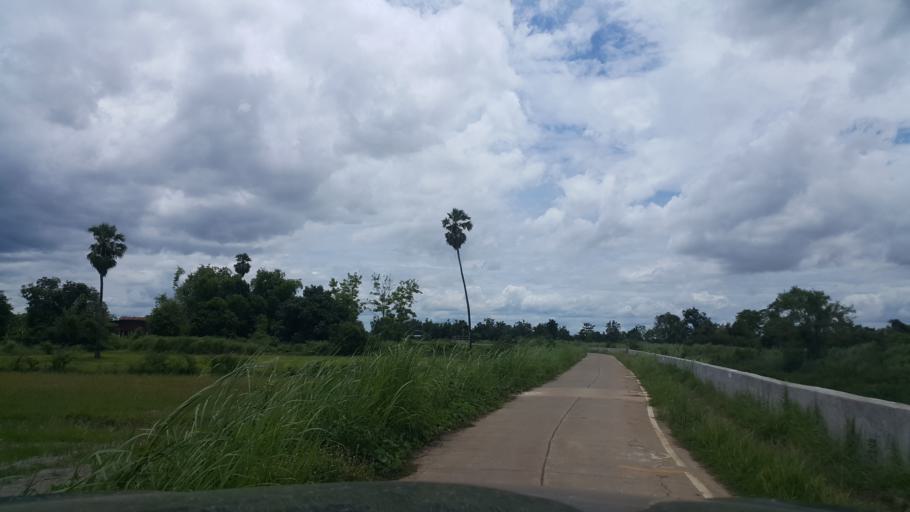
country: TH
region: Sukhothai
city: Sukhothai
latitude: 17.0214
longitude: 99.7998
